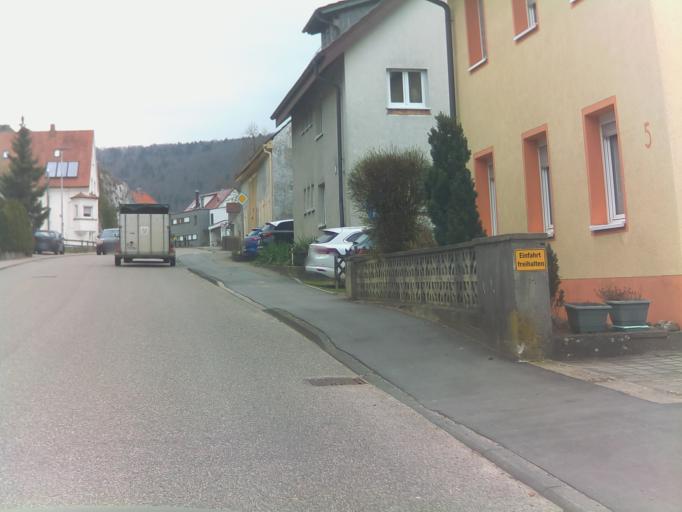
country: DE
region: Baden-Wuerttemberg
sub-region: Tuebingen Region
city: Schelklingen
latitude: 48.3771
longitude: 9.7312
